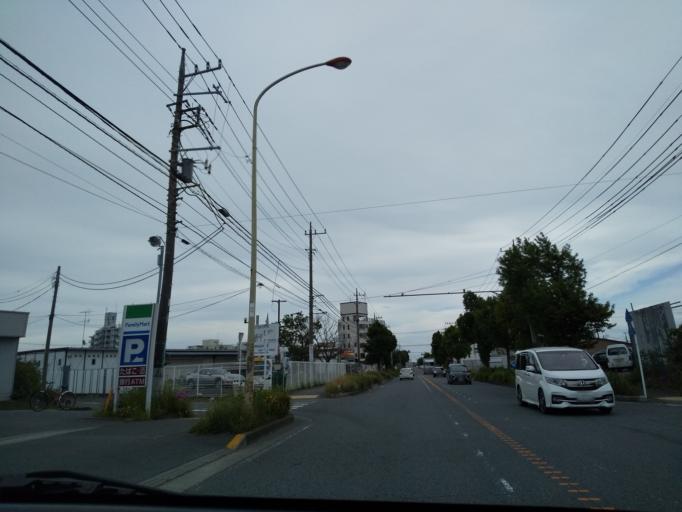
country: JP
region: Kanagawa
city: Zama
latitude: 35.5289
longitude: 139.3963
